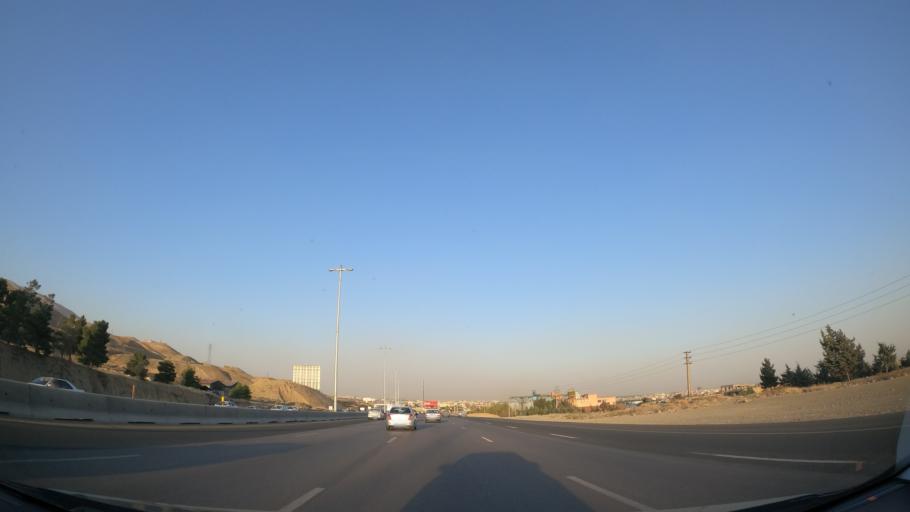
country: IR
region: Tehran
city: Shahr-e Qods
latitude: 35.7445
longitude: 51.0940
